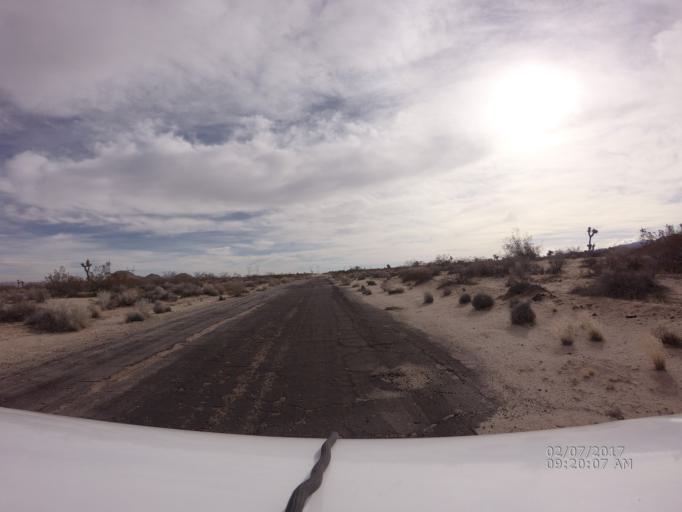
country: US
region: California
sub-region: San Bernardino County
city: Pinon Hills
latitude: 34.5276
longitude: -117.7247
